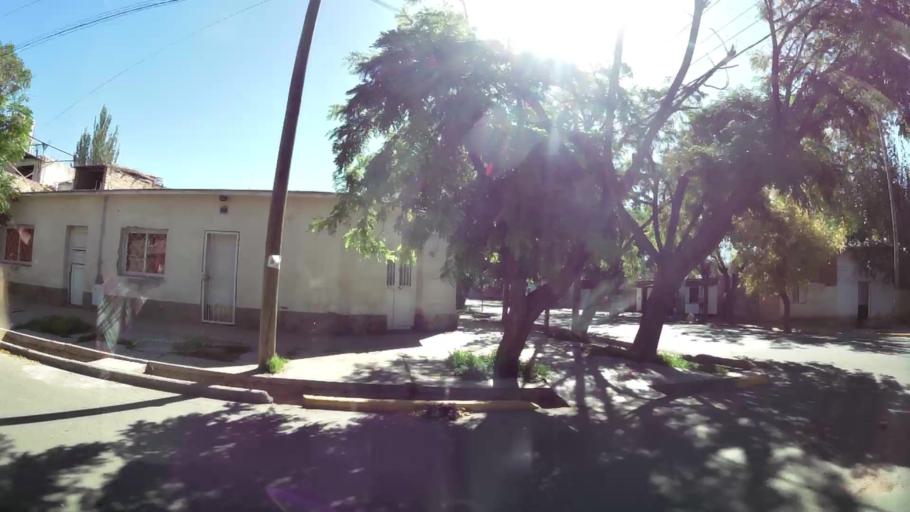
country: AR
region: Mendoza
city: Las Heras
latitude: -32.8410
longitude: -68.8234
